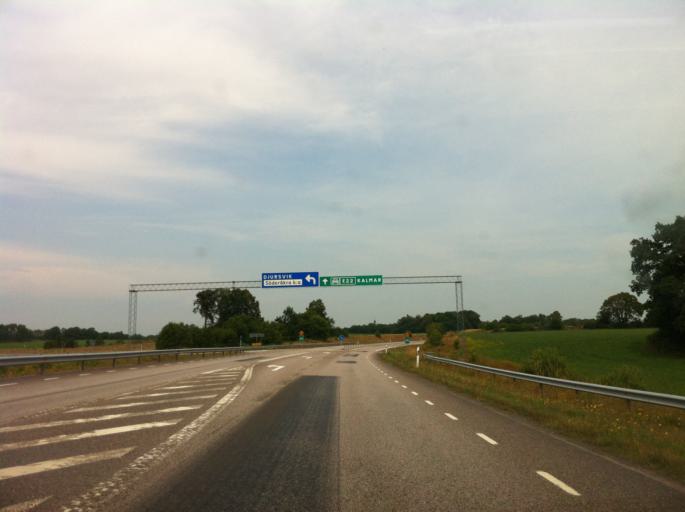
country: SE
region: Kalmar
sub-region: Torsas Kommun
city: Torsas
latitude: 56.4321
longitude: 16.0774
